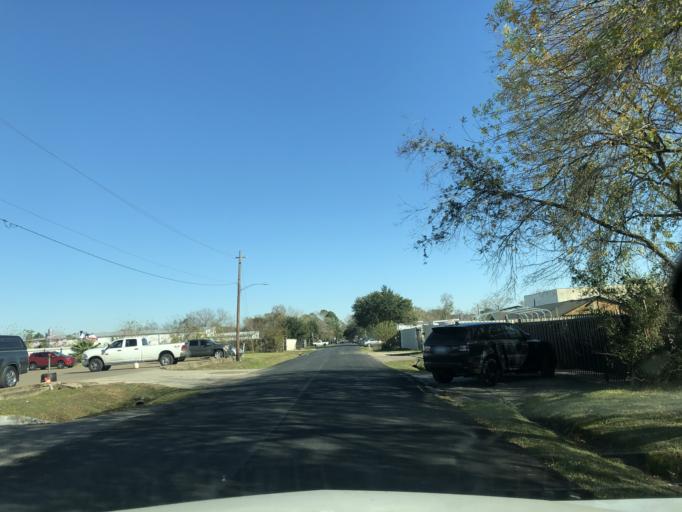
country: US
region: Texas
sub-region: Harris County
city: Bellaire
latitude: 29.6908
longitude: -95.4992
